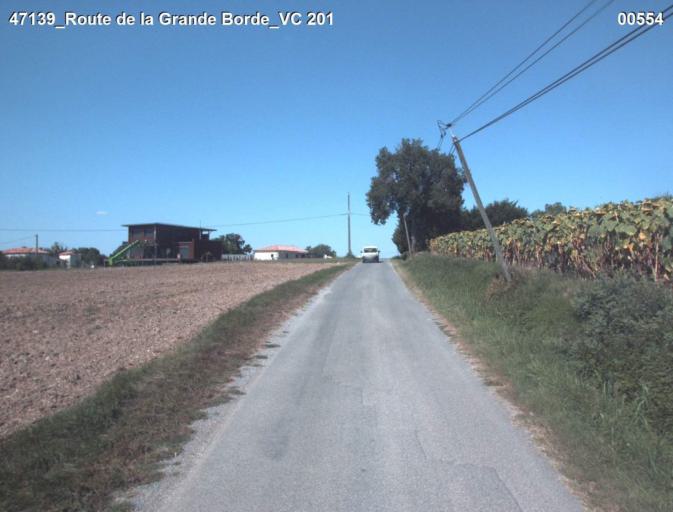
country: FR
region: Aquitaine
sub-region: Departement du Lot-et-Garonne
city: Nerac
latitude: 44.0672
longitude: 0.3926
